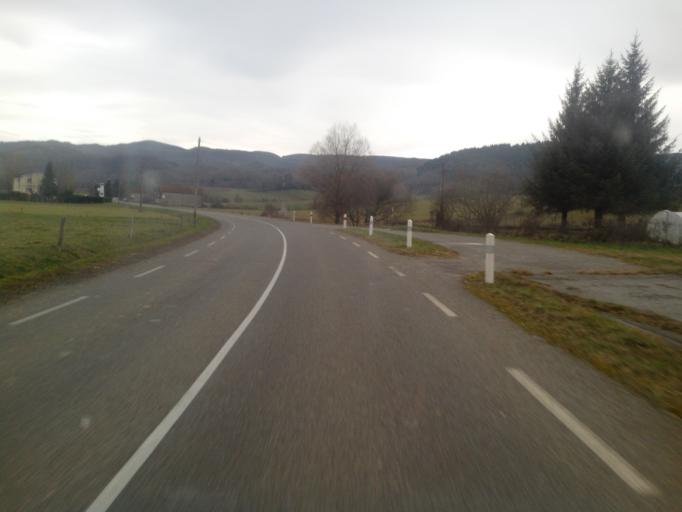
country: FR
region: Midi-Pyrenees
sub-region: Departement de l'Ariege
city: Foix
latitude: 43.0139
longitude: 1.4062
